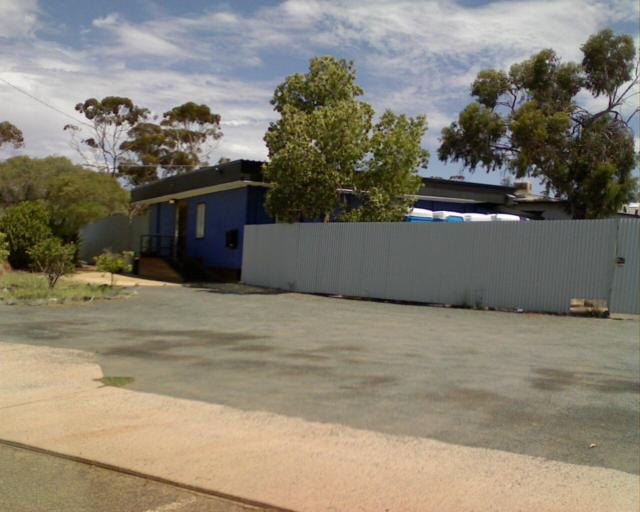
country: AU
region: Western Australia
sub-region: Kalgoorlie/Boulder
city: Stoneville
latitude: -31.2035
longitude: 121.6658
